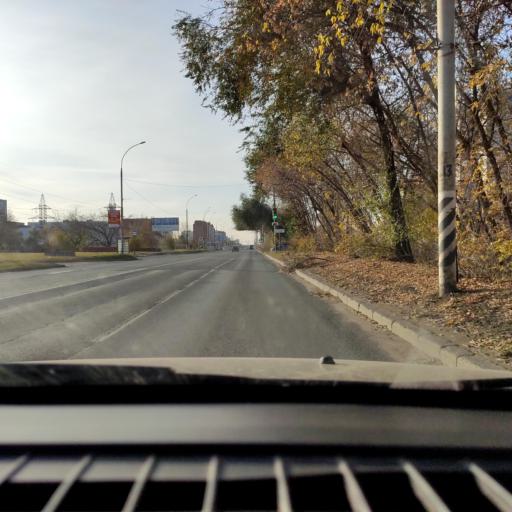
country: RU
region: Samara
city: Tol'yatti
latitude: 53.5469
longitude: 49.3169
